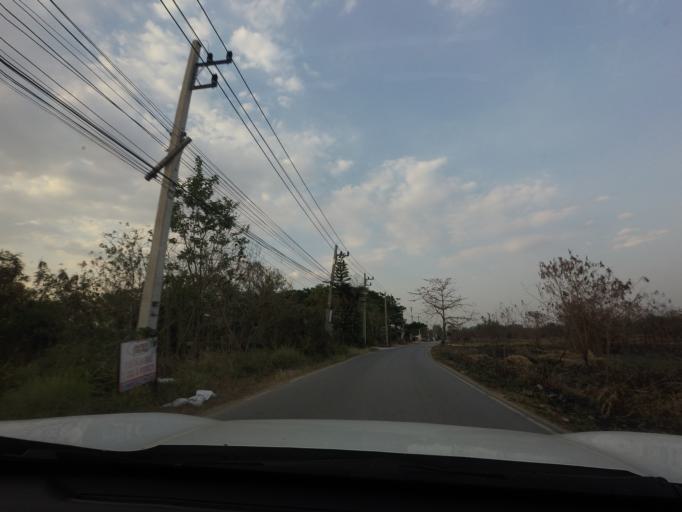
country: TH
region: Nakhon Ratchasima
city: Pak Chong
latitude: 14.6033
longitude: 101.4441
